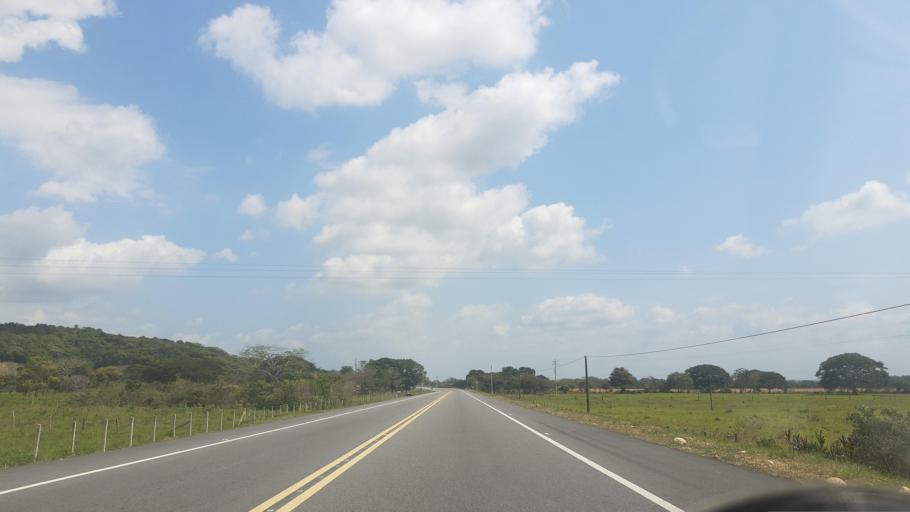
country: CO
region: Casanare
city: Tauramena
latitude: 4.8837
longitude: -72.6941
